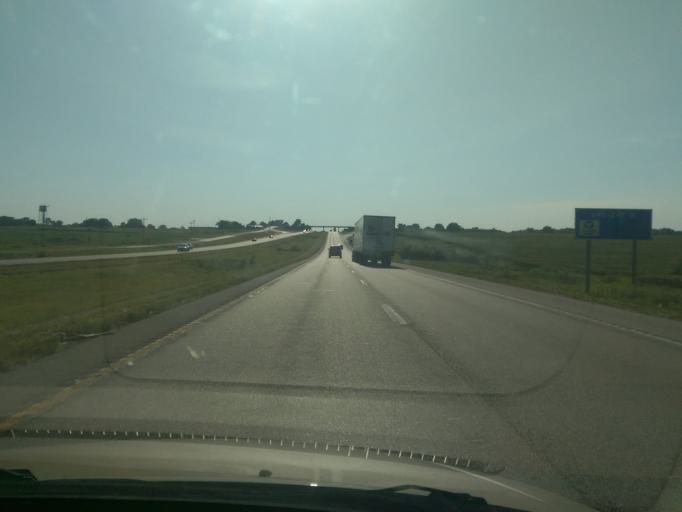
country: US
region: Missouri
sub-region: Jackson County
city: Oak Grove
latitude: 39.0114
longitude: -94.0601
